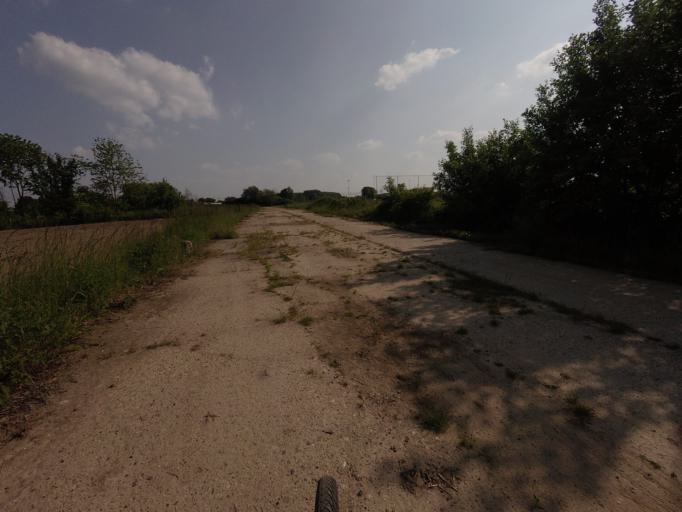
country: BE
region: Flanders
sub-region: Provincie Antwerpen
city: Borsbeek
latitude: 51.1823
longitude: 4.4729
